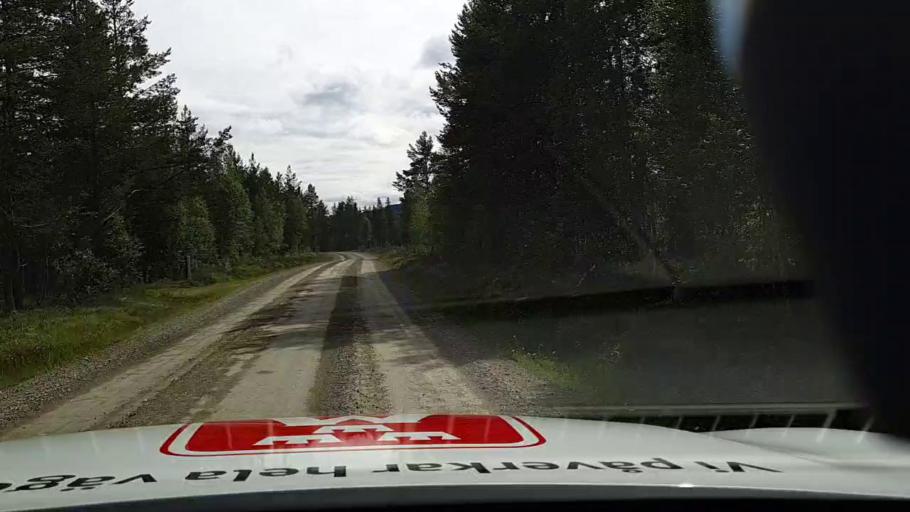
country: SE
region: Jaemtland
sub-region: Are Kommun
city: Jarpen
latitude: 62.5007
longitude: 13.5016
